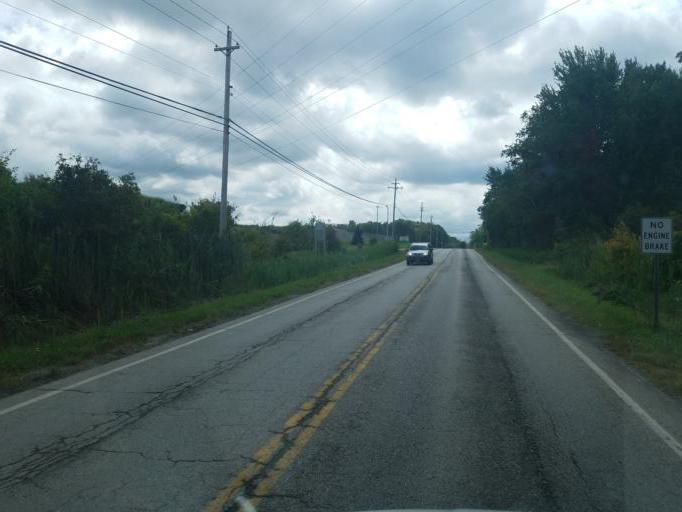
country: US
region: Ohio
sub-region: Lake County
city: Perry
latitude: 41.7053
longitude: -81.1762
